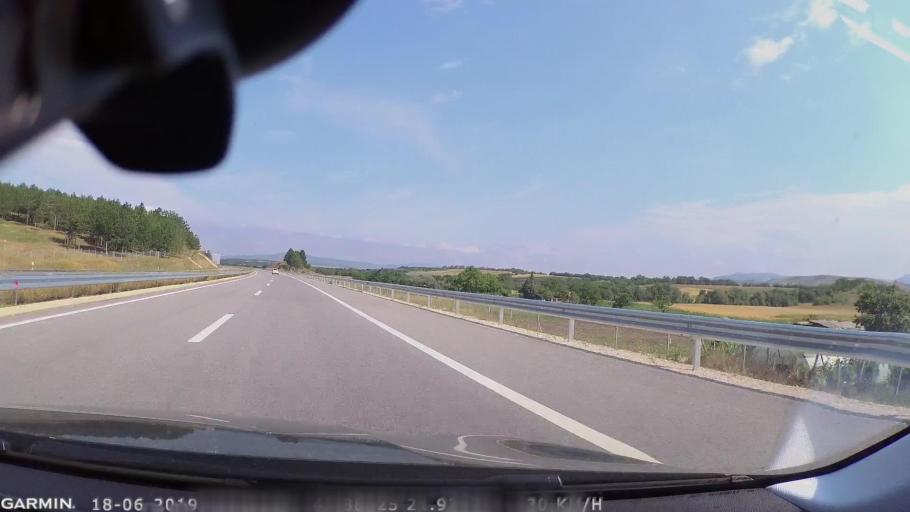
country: MK
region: Sveti Nikole
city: Sveti Nikole
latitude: 41.8871
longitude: 21.9321
